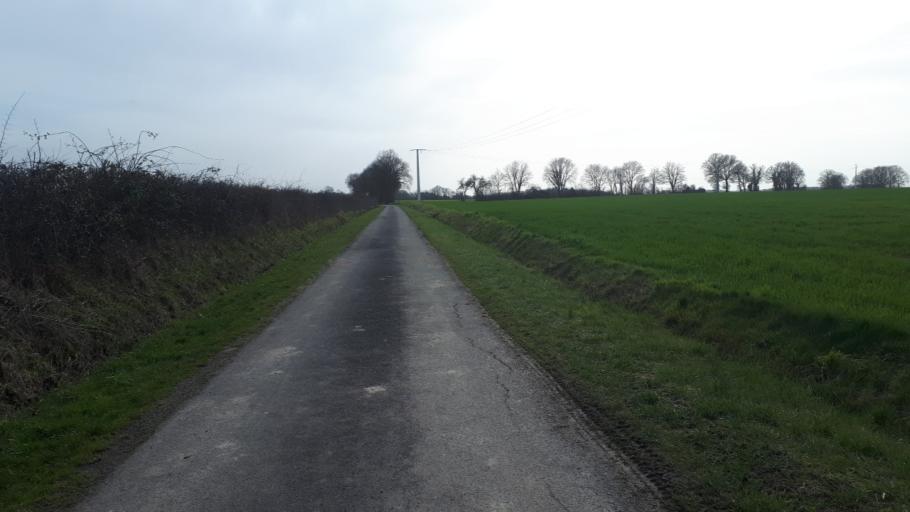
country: FR
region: Poitou-Charentes
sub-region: Departement de la Vienne
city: Archigny
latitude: 46.6340
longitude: 0.7482
